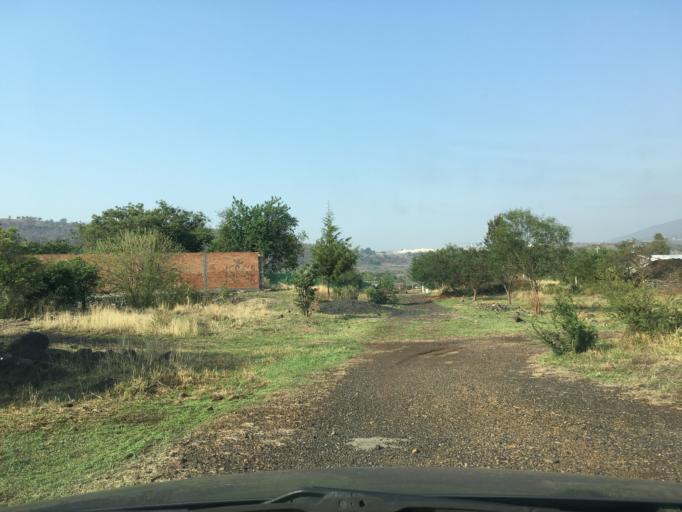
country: MX
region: Michoacan
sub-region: Morelia
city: La Mintzita (Piedra Dura)
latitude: 19.6469
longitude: -101.2786
